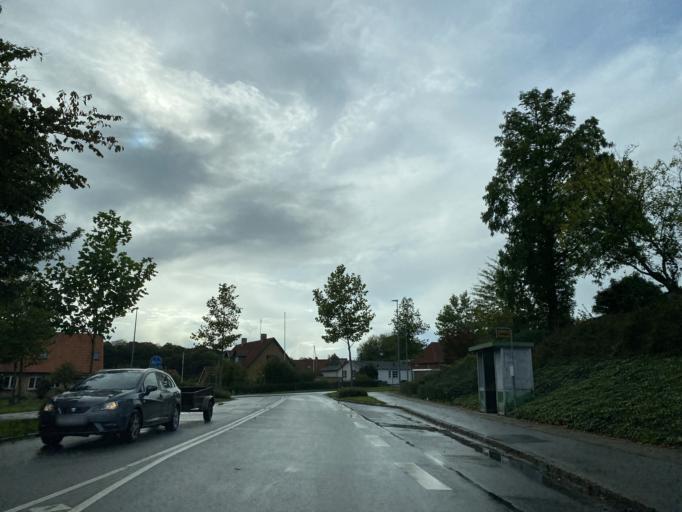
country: DK
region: South Denmark
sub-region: Haderslev Kommune
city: Haderslev
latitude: 55.2528
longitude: 9.4598
